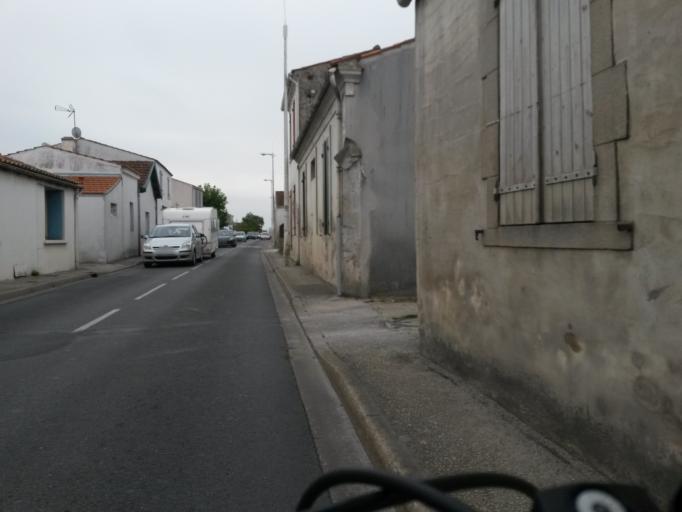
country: FR
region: Poitou-Charentes
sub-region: Departement de la Charente-Maritime
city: Dolus-d'Oleron
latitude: 45.9427
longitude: -1.3156
